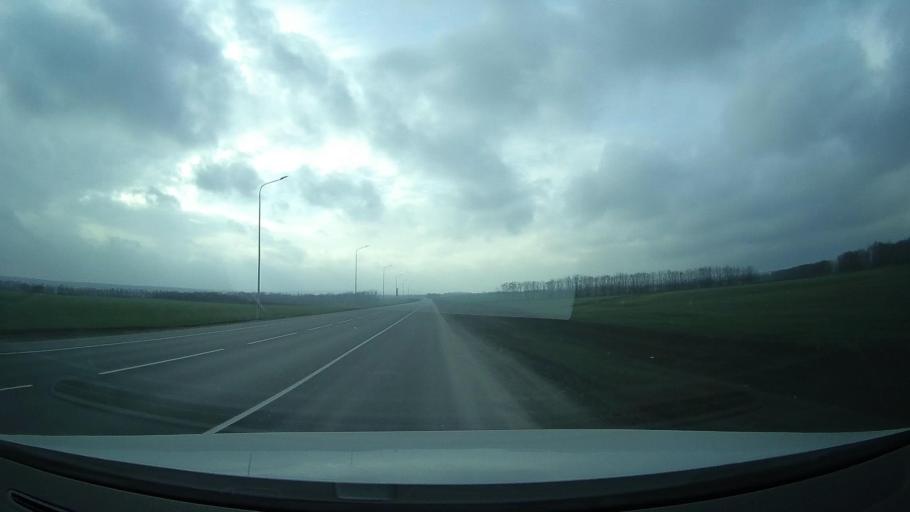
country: RU
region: Rostov
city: Grushevskaya
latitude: 47.4734
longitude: 39.9078
